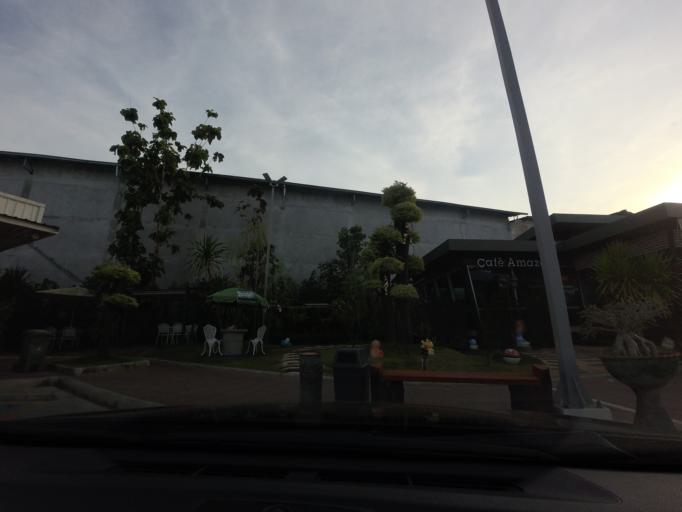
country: TH
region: Narathiwat
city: Narathiwat
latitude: 6.4080
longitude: 101.7954
